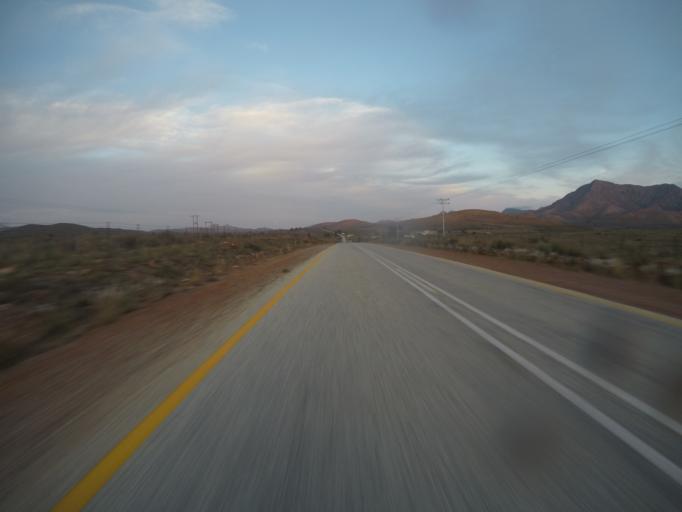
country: ZA
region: Western Cape
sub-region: Eden District Municipality
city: Plettenberg Bay
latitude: -33.7310
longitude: 23.3982
